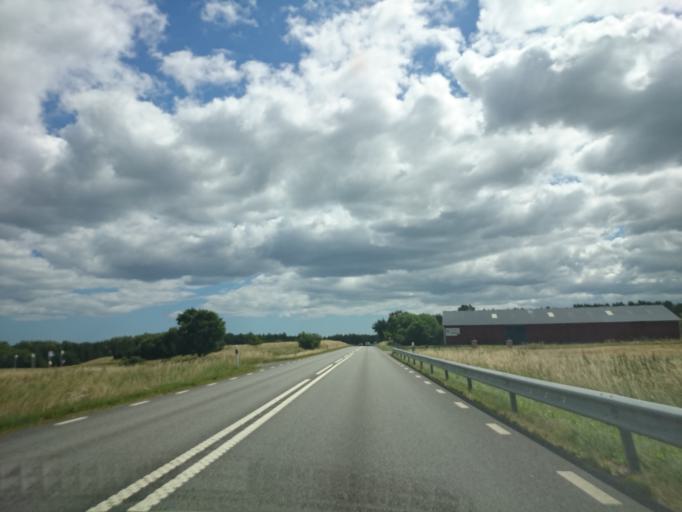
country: SE
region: Skane
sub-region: Kristianstads Kommun
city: Degeberga
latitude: 55.8191
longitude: 14.1241
